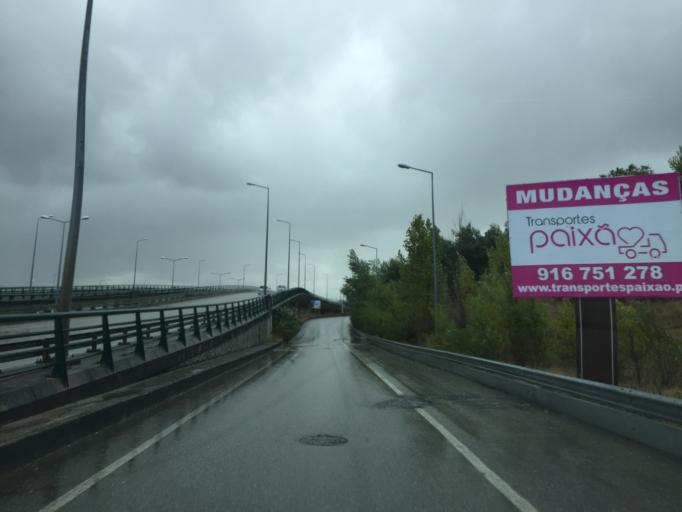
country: PT
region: Coimbra
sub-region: Coimbra
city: Coimbra
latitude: 40.2131
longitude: -8.4414
